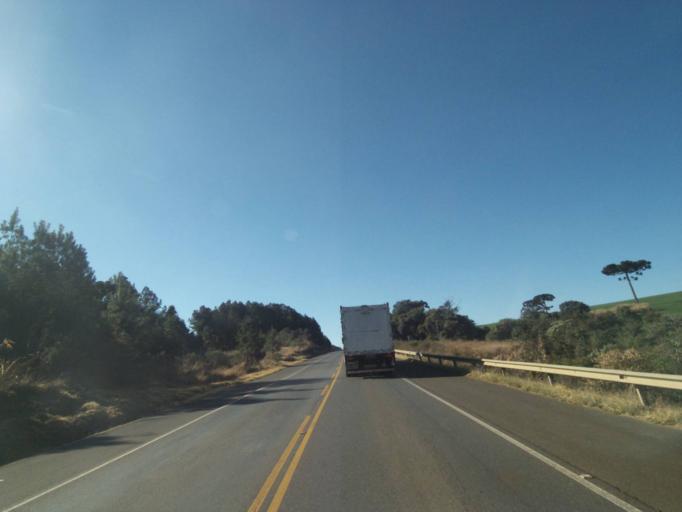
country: BR
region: Parana
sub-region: Tibagi
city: Tibagi
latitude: -24.5463
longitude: -50.4509
